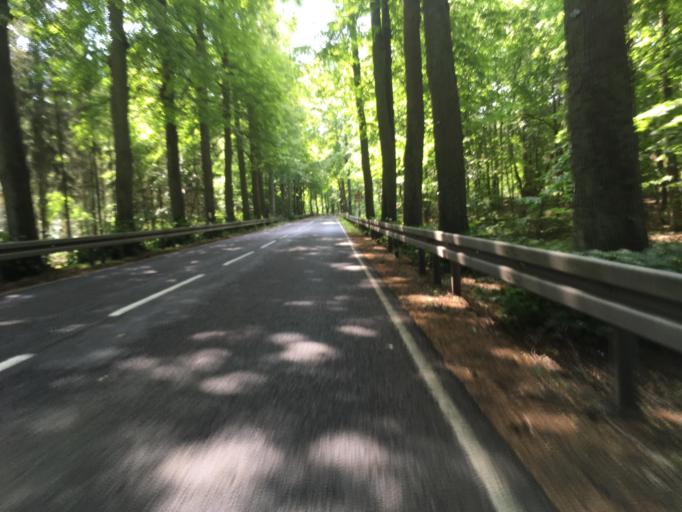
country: DE
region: Brandenburg
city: Friedrichswalde
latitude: 53.0811
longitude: 13.7220
